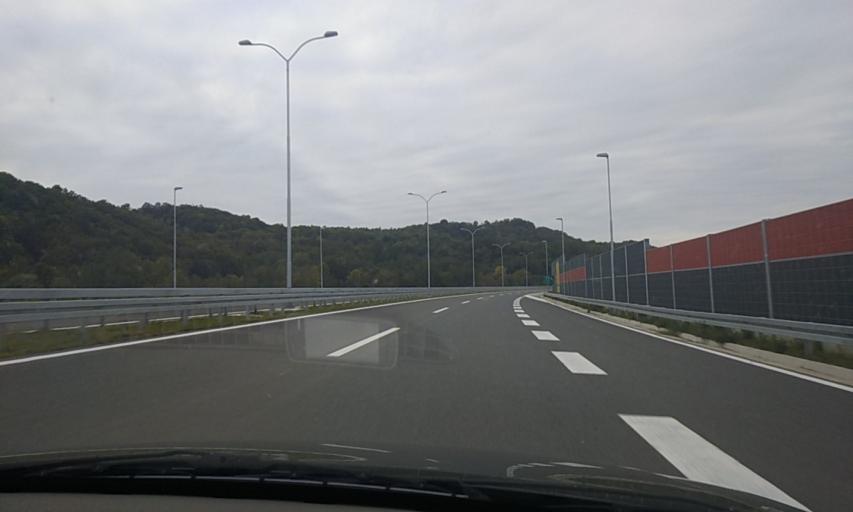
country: BA
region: Republika Srpska
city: Maglajani
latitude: 44.8711
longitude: 17.3989
